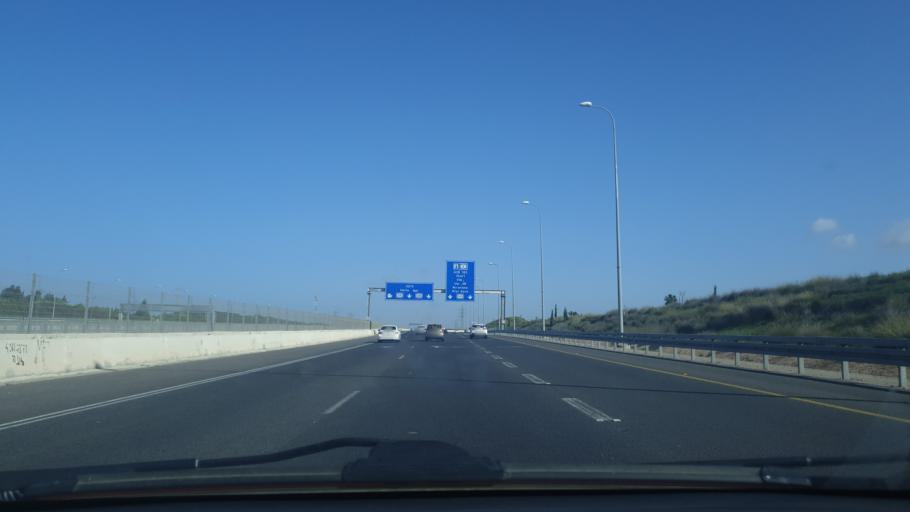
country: IL
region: Tel Aviv
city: Kefar Shemaryahu
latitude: 32.1866
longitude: 34.8289
